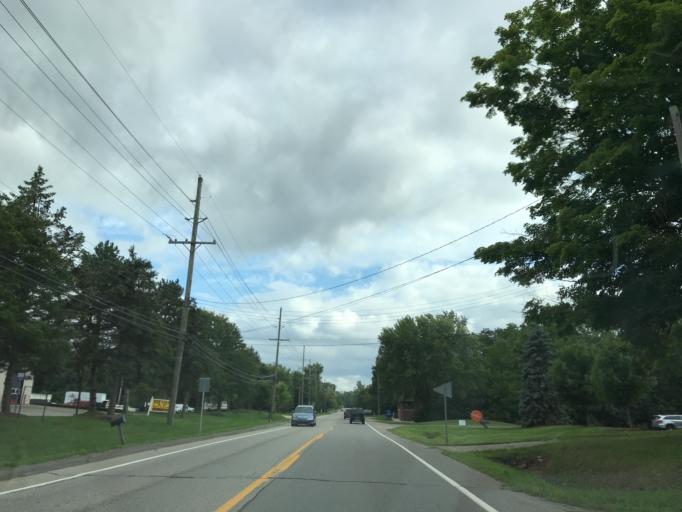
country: US
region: Michigan
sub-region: Wayne County
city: Northville
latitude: 42.4098
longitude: -83.4692
